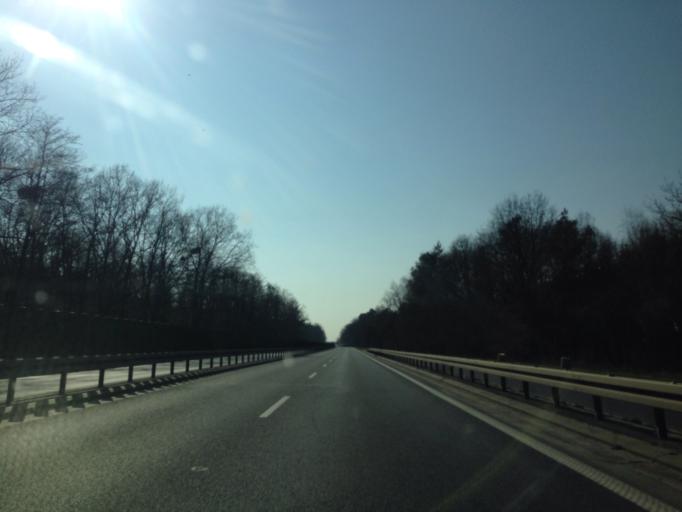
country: PL
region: Lower Silesian Voivodeship
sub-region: Powiat wroclawski
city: Dlugoleka
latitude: 51.1932
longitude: 17.2608
